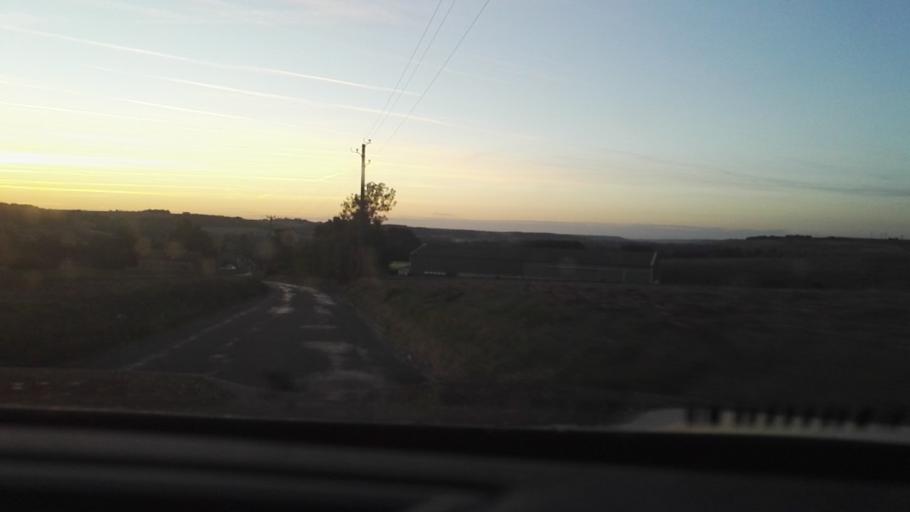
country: FR
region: Haute-Normandie
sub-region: Departement de l'Eure
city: Breuilpont
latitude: 48.9776
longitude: 1.4293
